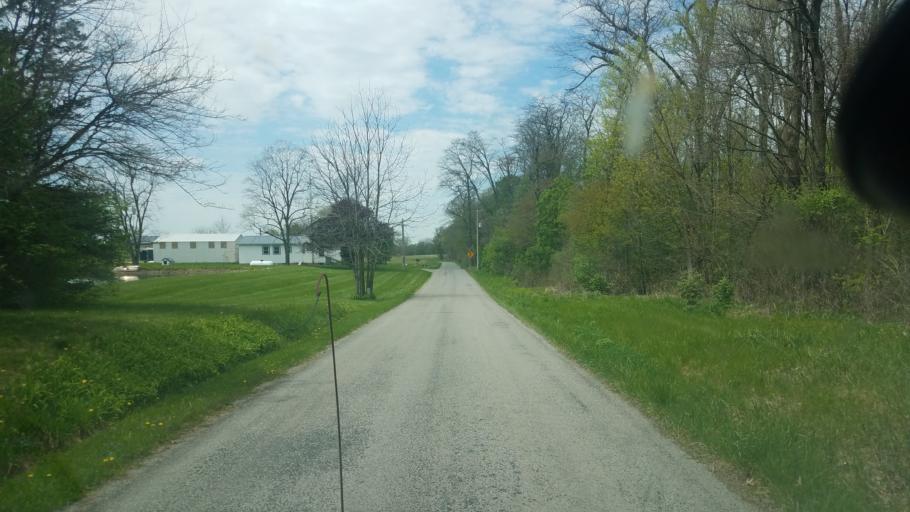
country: US
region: Ohio
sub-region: Hardin County
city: Ada
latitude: 40.7906
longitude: -83.8836
